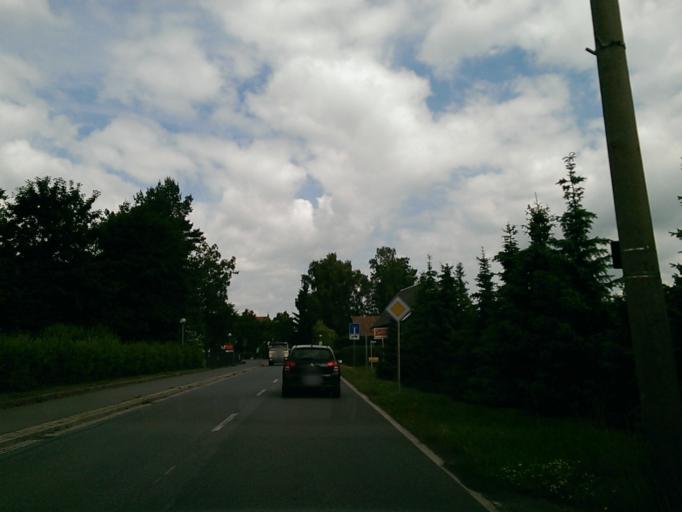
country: DE
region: Saxony
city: Mittelherwigsdorf
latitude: 50.9485
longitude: 14.7358
